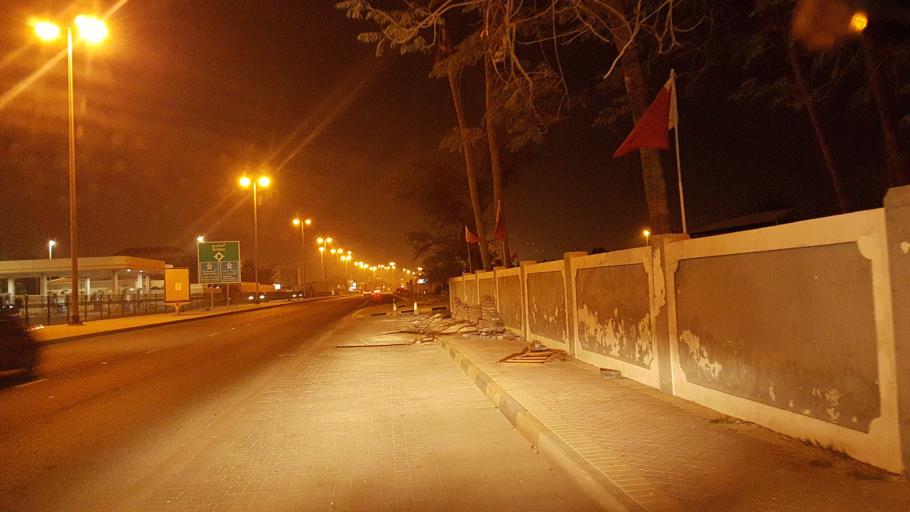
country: BH
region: Manama
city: Jidd Hafs
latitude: 26.2189
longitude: 50.5265
